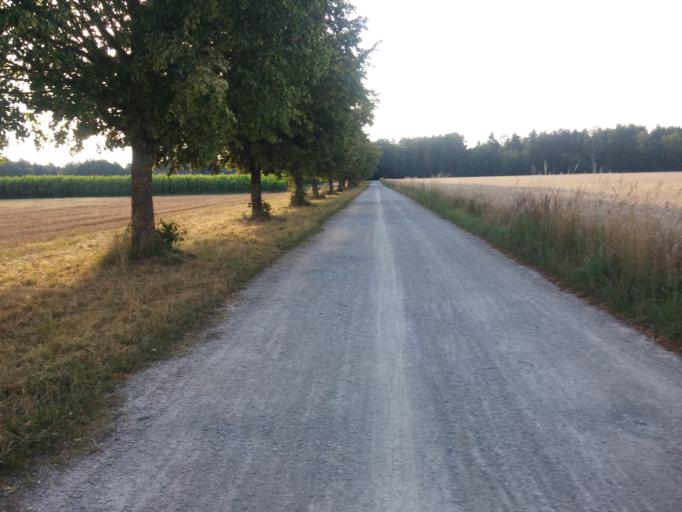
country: DE
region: Bavaria
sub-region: Upper Bavaria
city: Grasbrunn
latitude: 48.0620
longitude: 11.7644
